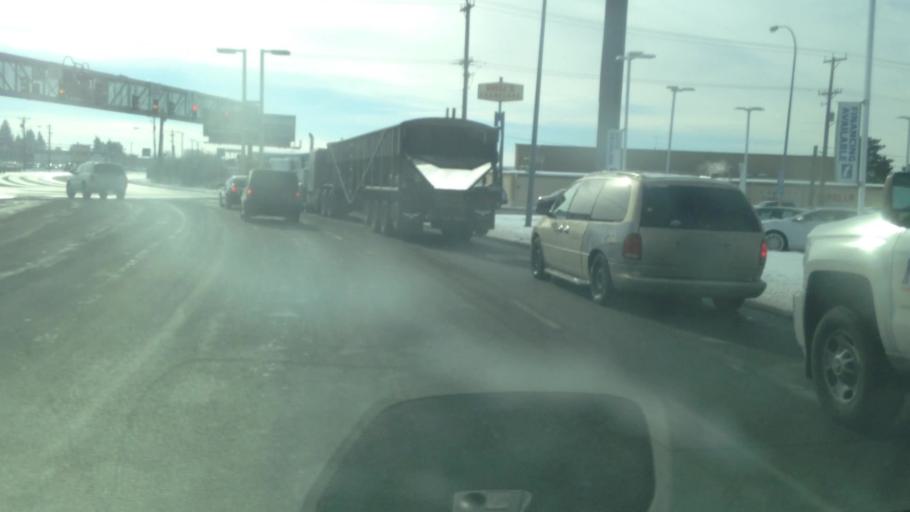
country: US
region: Idaho
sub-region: Bonneville County
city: Idaho Falls
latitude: 43.5120
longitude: -112.0241
